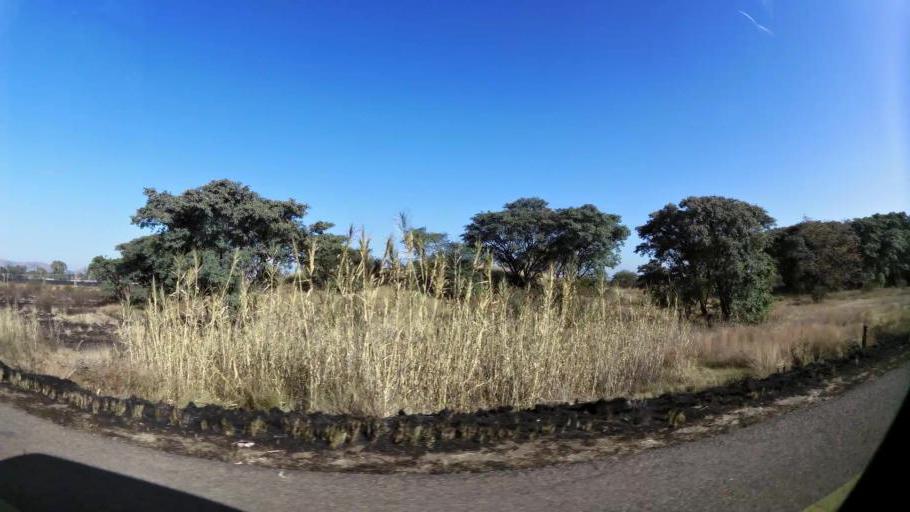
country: ZA
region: North-West
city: Ga-Rankuwa
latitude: -25.6341
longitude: 28.1108
